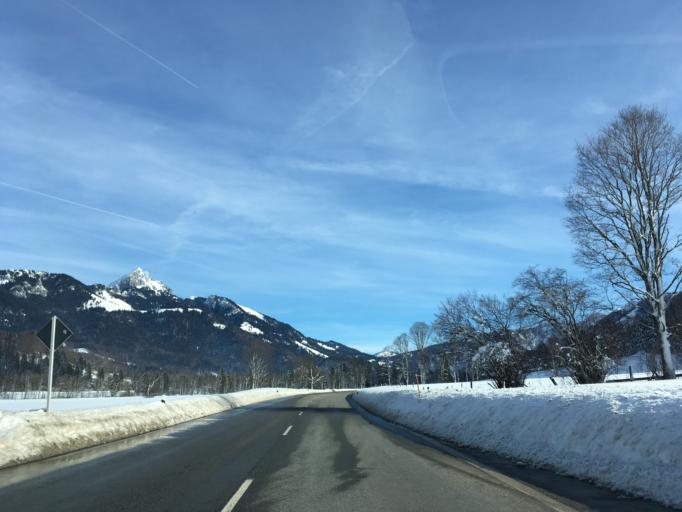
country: DE
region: Bavaria
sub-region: Upper Bavaria
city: Fischbachau
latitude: 47.7002
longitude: 11.9382
